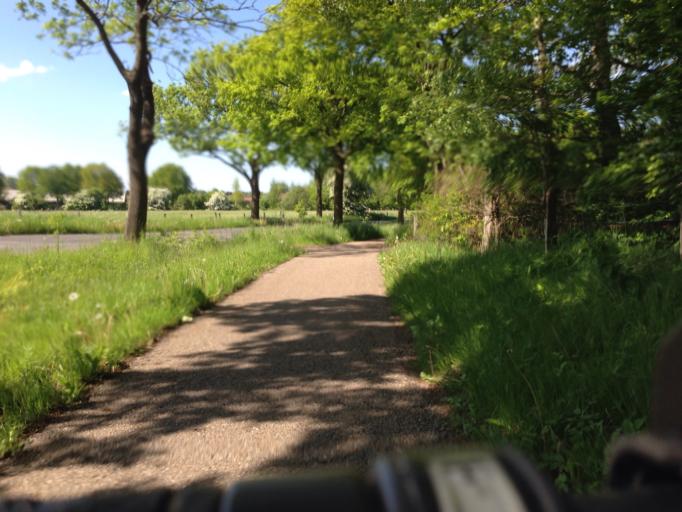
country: DE
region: Schleswig-Holstein
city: Stapelfeld
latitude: 53.5974
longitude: 10.2225
